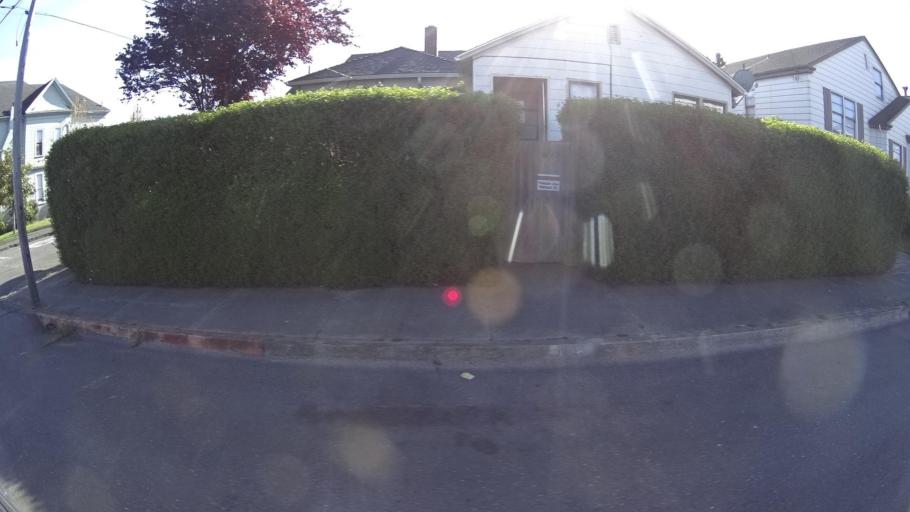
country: US
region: California
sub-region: Humboldt County
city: Eureka
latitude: 40.7925
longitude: -124.1648
